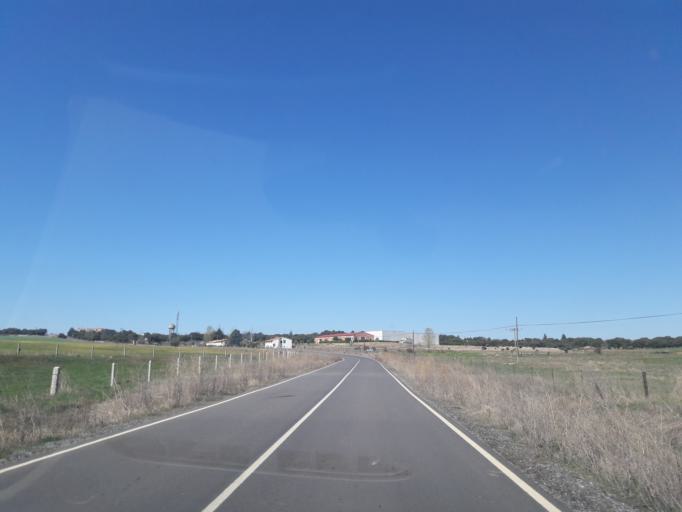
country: ES
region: Castille and Leon
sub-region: Provincia de Salamanca
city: Martinamor
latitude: 40.8099
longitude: -5.6217
